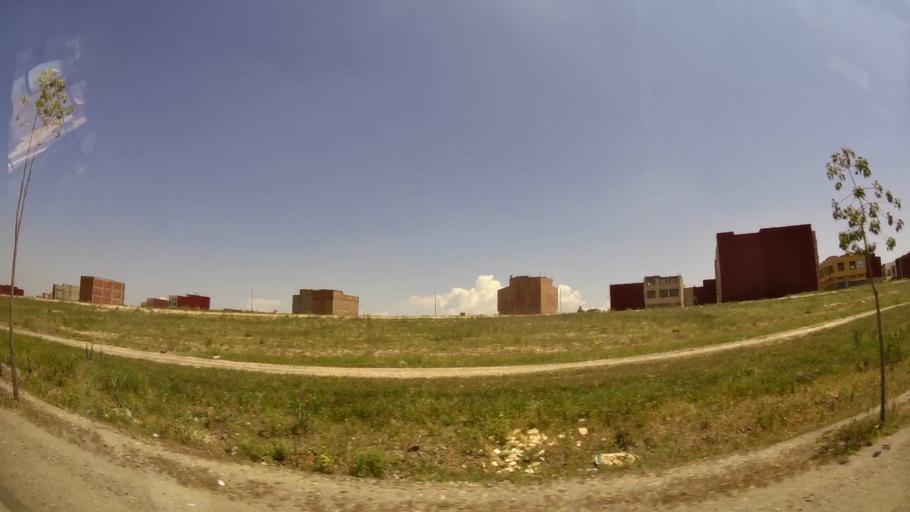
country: MA
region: Oriental
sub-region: Oujda-Angad
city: Oujda
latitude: 34.6607
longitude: -1.9546
